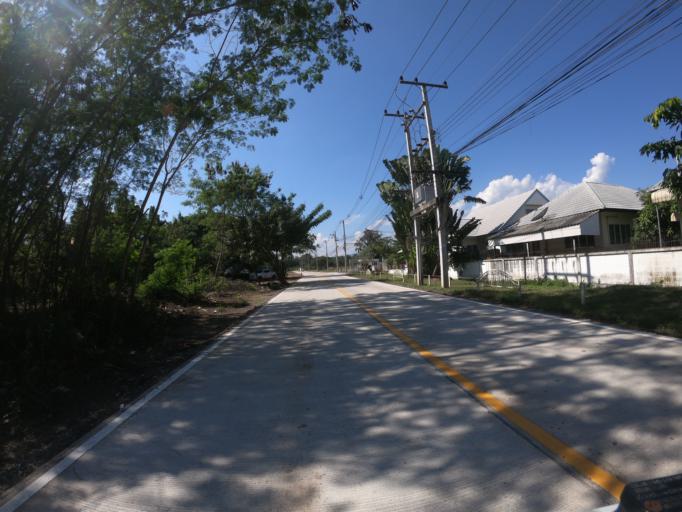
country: TH
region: Chiang Mai
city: Chiang Mai
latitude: 18.7441
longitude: 98.9668
